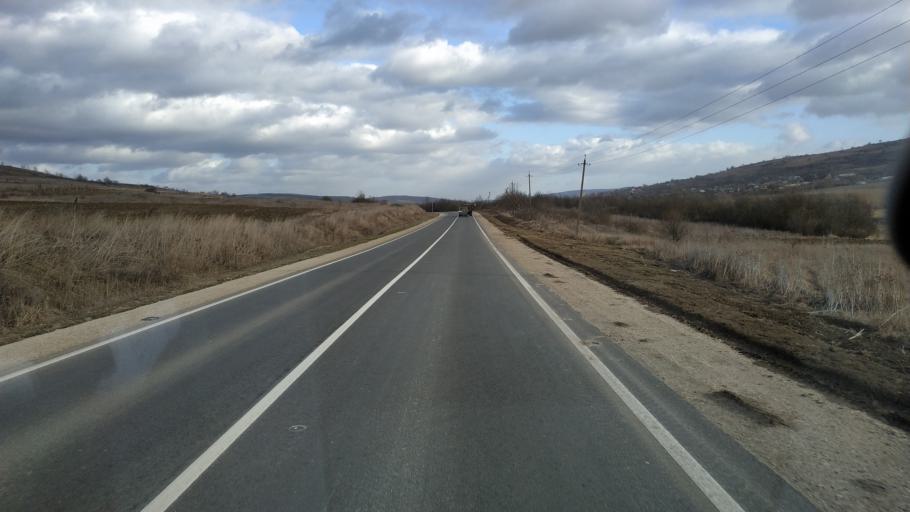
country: MD
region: Calarasi
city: Calarasi
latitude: 47.2939
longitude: 28.1706
